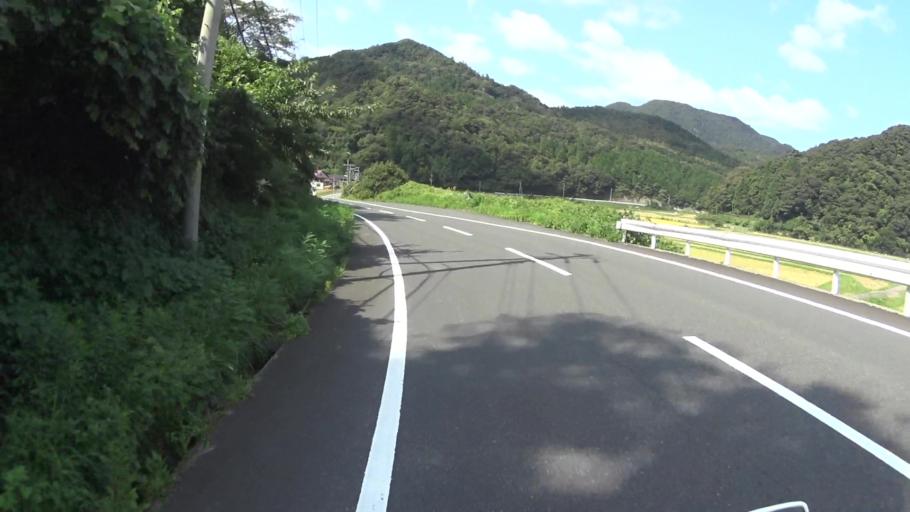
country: JP
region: Kyoto
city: Miyazu
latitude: 35.7088
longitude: 135.2532
